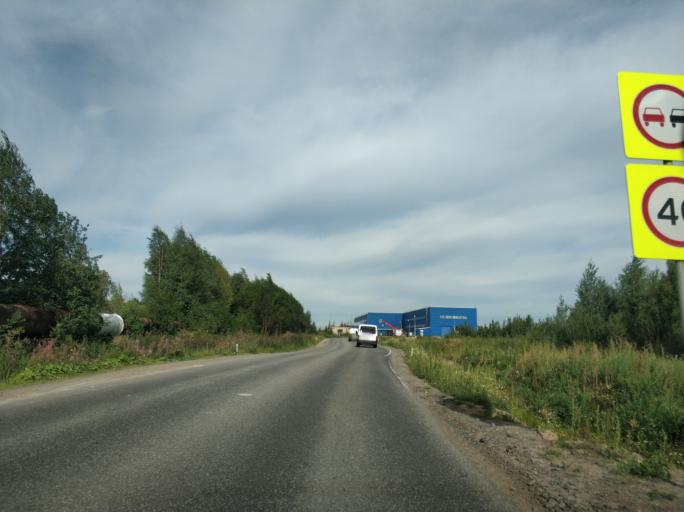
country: RU
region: St.-Petersburg
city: Grazhdanka
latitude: 60.0471
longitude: 30.4148
